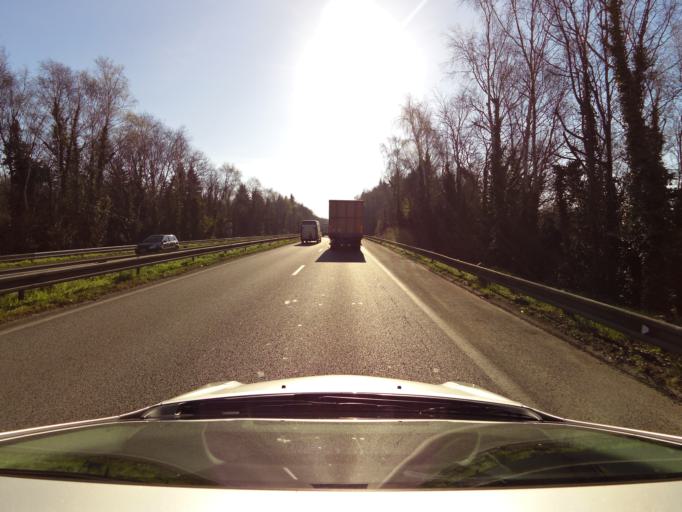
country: FR
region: Brittany
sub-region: Departement du Morbihan
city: Hennebont
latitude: 47.7894
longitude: -3.2914
